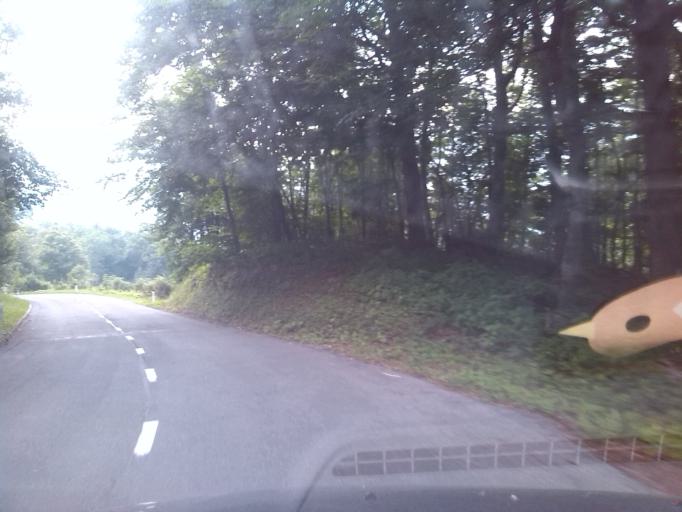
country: SI
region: Kobarid
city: Kobarid
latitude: 46.2173
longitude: 13.5959
